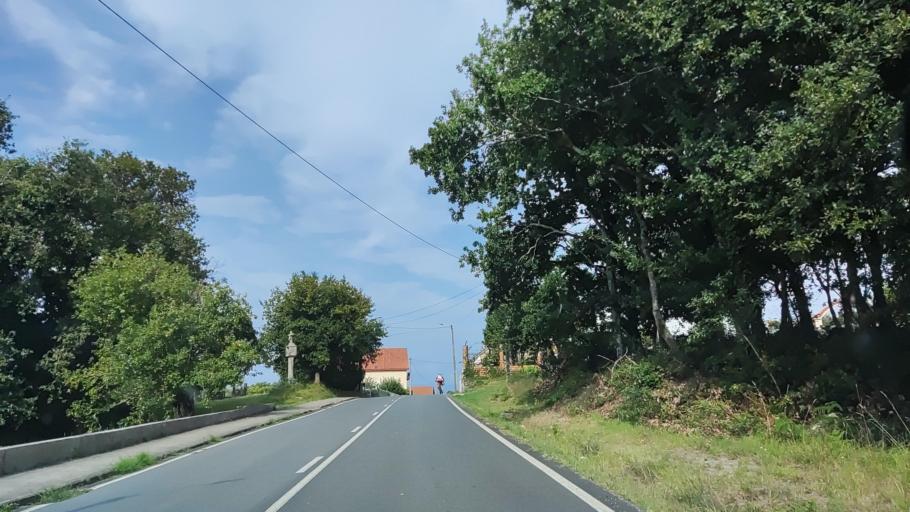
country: ES
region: Galicia
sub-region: Provincia da Coruna
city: Rianxo
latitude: 42.6474
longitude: -8.7905
